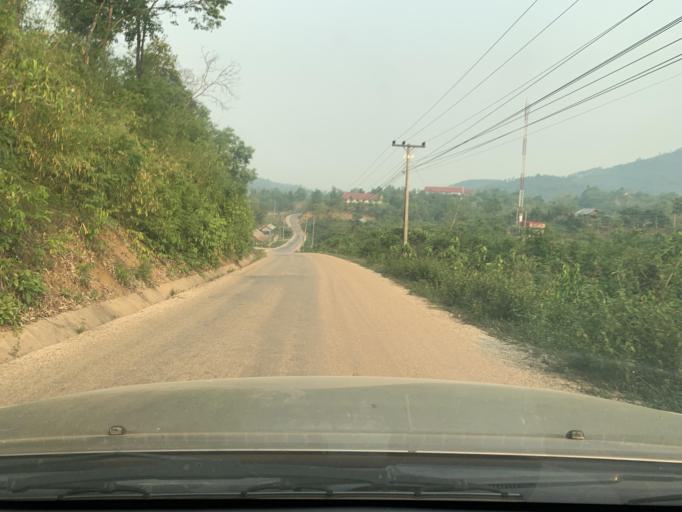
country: LA
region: Louangphabang
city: Louangphabang
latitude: 19.9108
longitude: 102.0804
